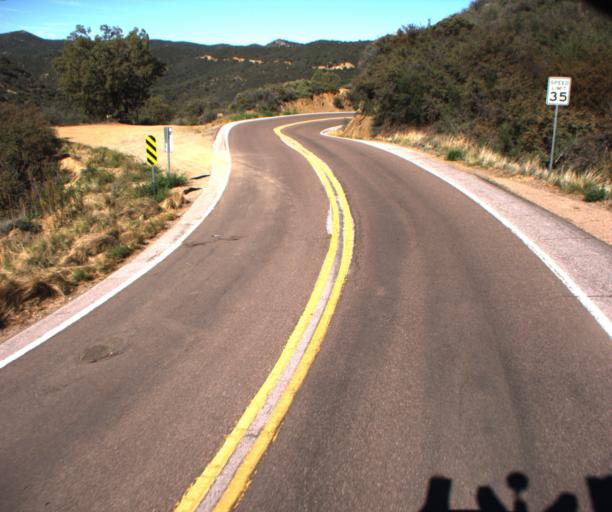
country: US
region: Arizona
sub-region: Yavapai County
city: Prescott
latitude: 34.4538
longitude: -112.5257
